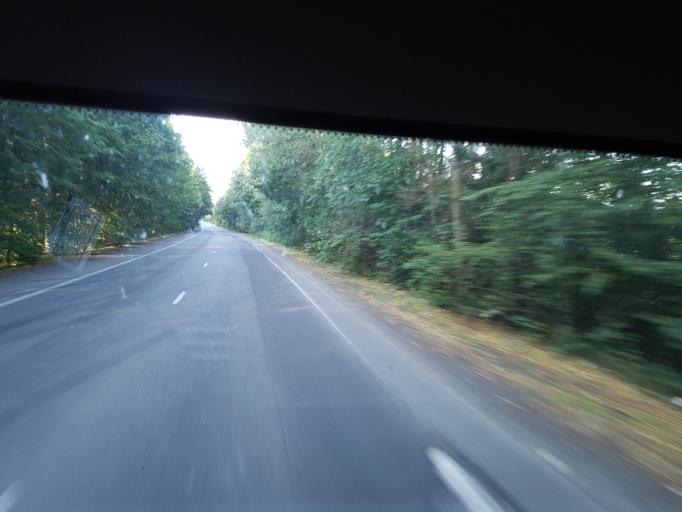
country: BE
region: Wallonia
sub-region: Province du Hainaut
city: Antoing
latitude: 50.5516
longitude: 3.4384
